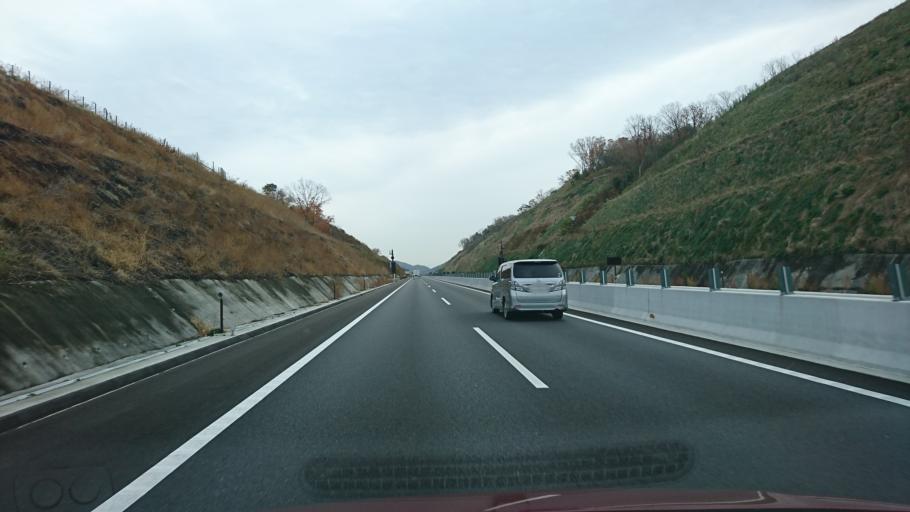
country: JP
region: Hyogo
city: Sandacho
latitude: 34.8644
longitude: 135.2810
